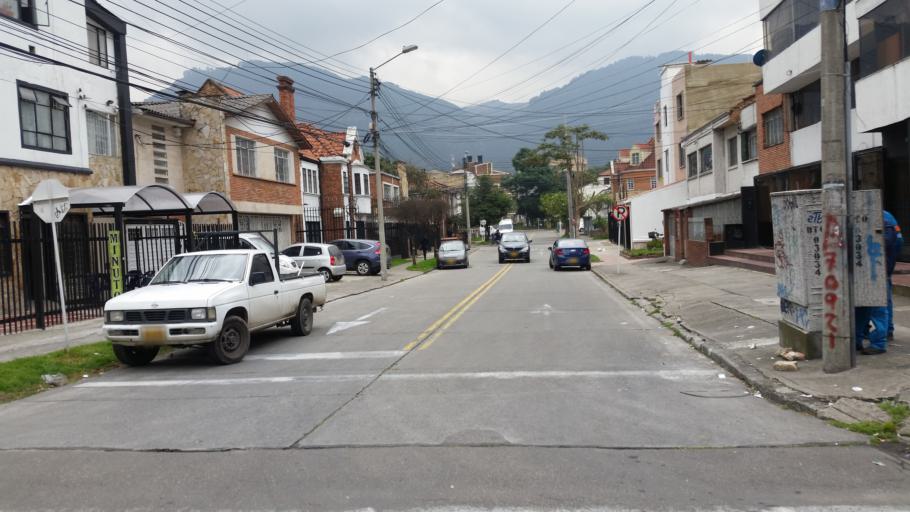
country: CO
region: Bogota D.C.
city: Bogota
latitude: 4.6248
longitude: -74.0749
